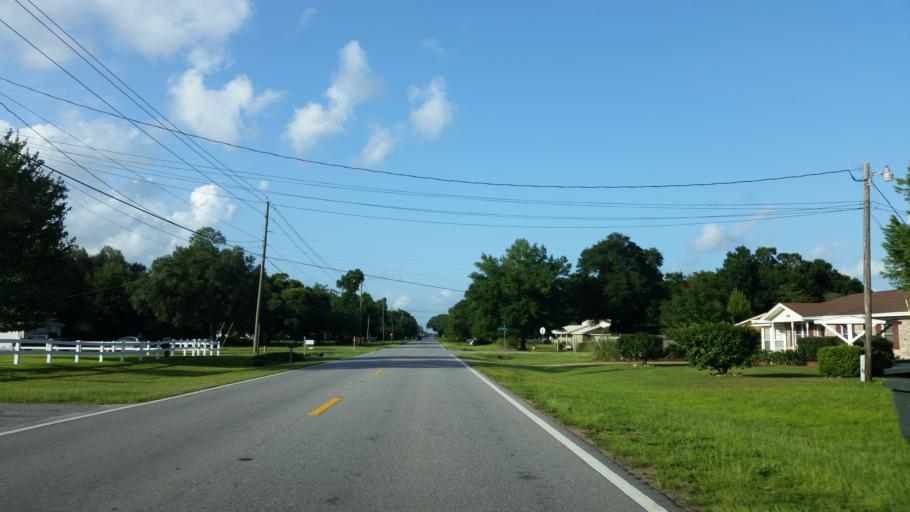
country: US
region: Florida
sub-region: Santa Rosa County
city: Bagdad
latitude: 30.5799
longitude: -87.0925
